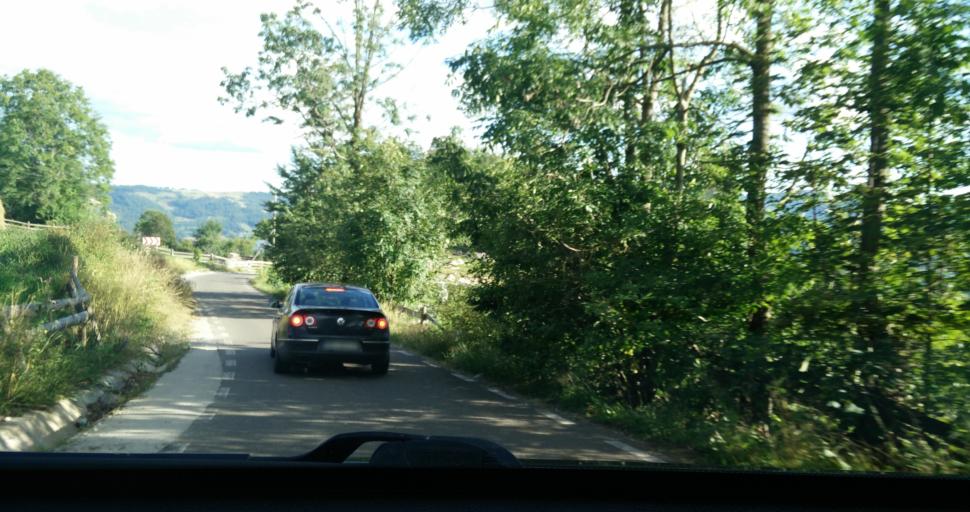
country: RO
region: Alba
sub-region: Comuna Scarisoara
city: Scarisoara
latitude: 46.4754
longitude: 22.8302
